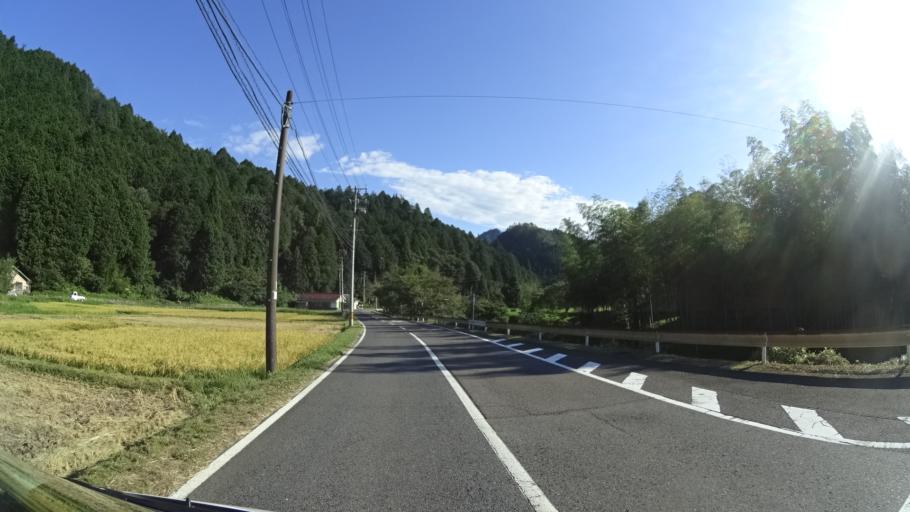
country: JP
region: Gifu
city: Minokamo
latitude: 35.5680
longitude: 137.0836
